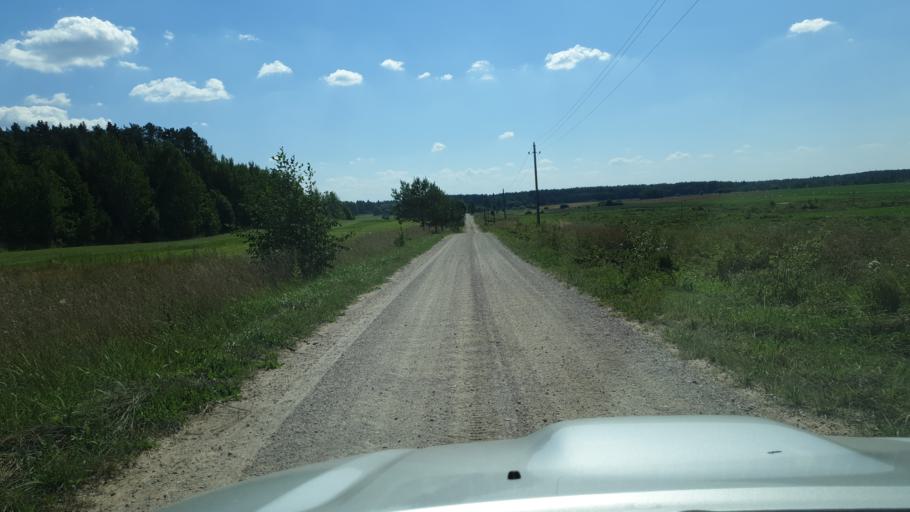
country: LT
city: Sirvintos
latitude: 54.9113
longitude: 24.9119
